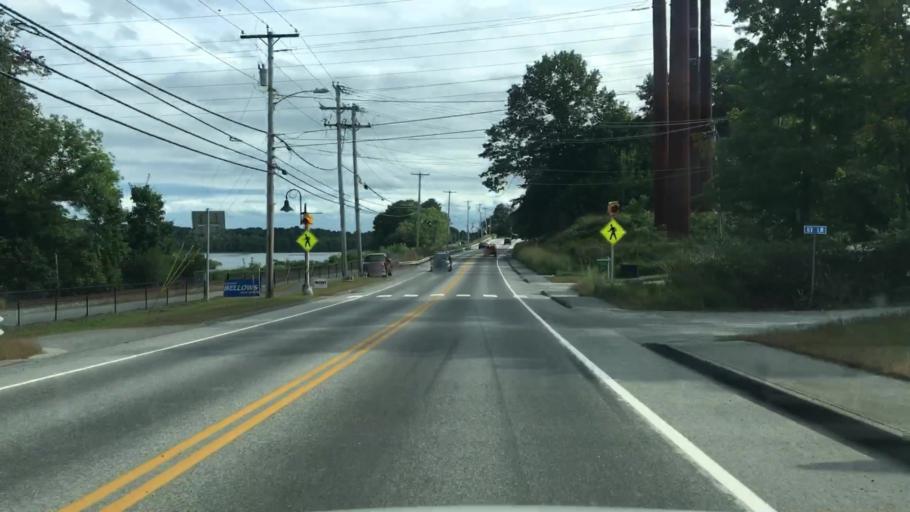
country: US
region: Maine
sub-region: Kennebec County
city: Farmingdale
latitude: 44.2539
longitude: -69.7727
